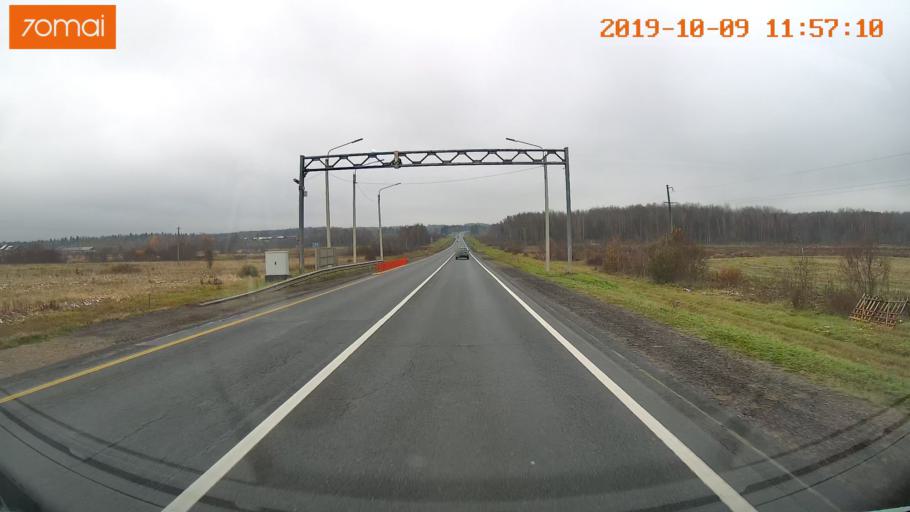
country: RU
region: Vologda
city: Gryazovets
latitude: 58.7357
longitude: 40.2911
